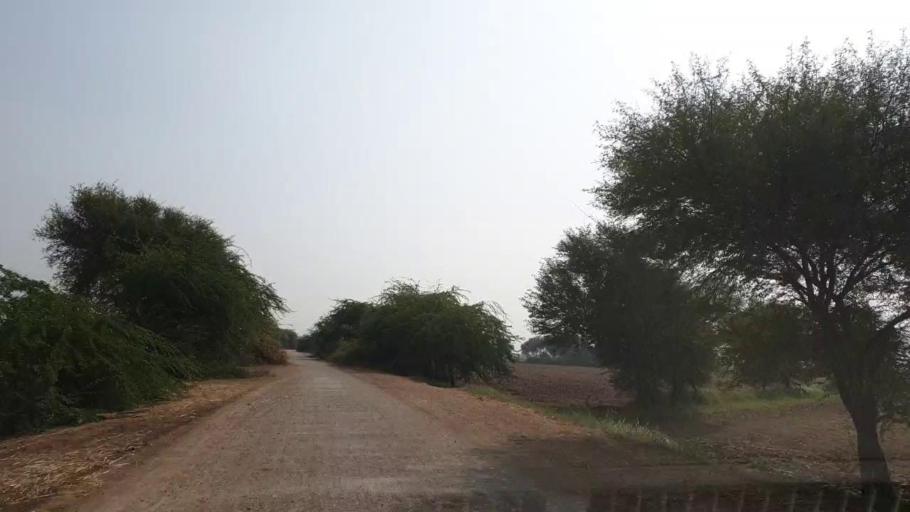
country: PK
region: Sindh
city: Matli
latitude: 24.9930
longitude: 68.5772
